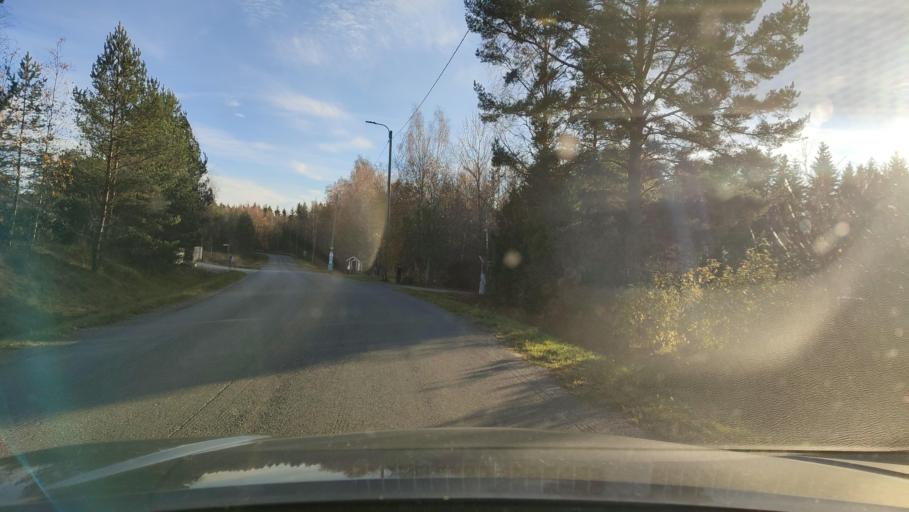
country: FI
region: Ostrobothnia
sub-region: Vaasa
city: Teeriniemi
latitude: 63.0695
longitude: 21.6897
